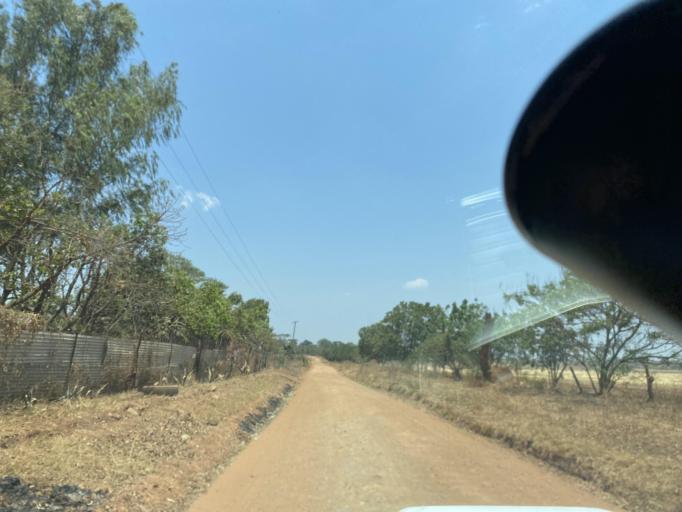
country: ZM
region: Lusaka
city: Lusaka
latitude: -15.4465
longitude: 28.0498
